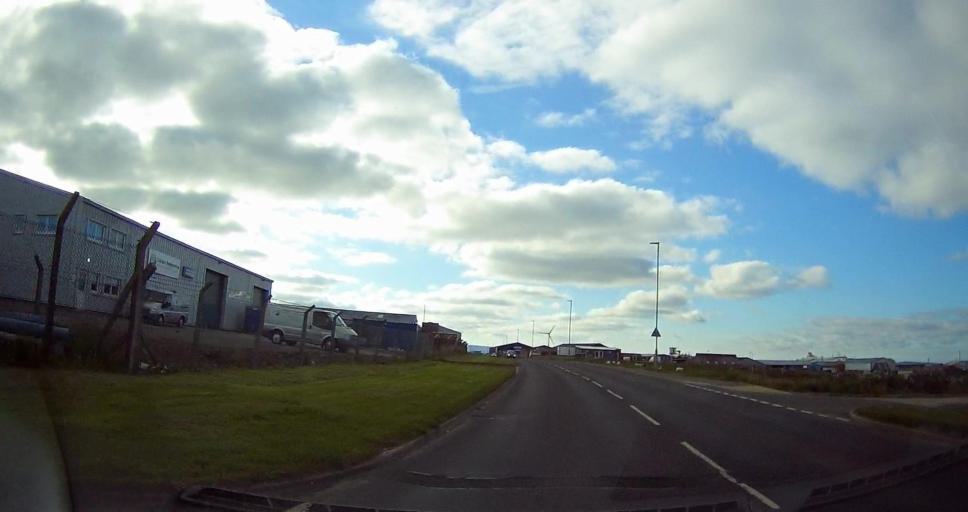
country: GB
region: Scotland
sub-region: Orkney Islands
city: Orkney
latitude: 58.9895
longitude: -2.9706
